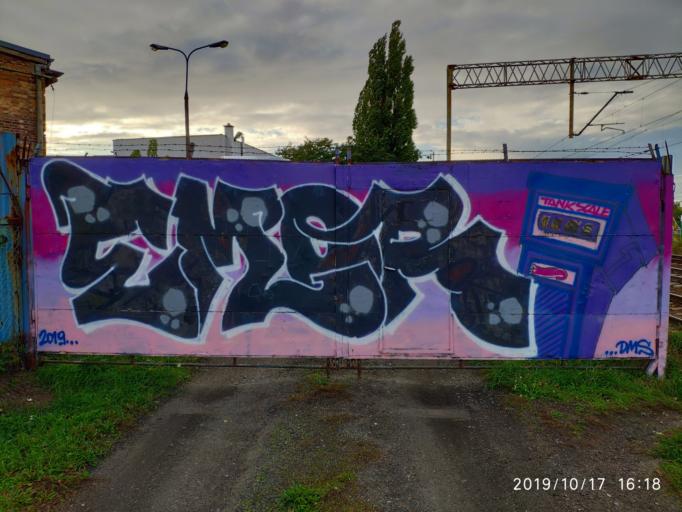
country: PL
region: Lubusz
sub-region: Zielona Gora
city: Zielona Gora
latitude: 51.9493
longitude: 15.4891
